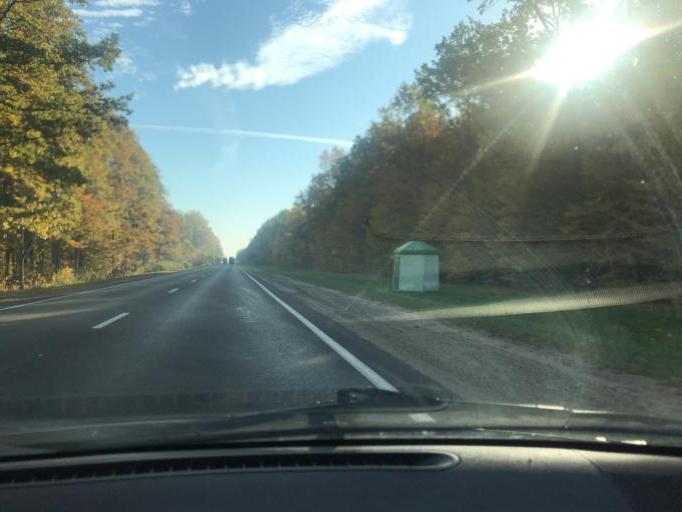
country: BY
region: Brest
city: Ivanava
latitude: 52.1530
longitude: 25.3593
